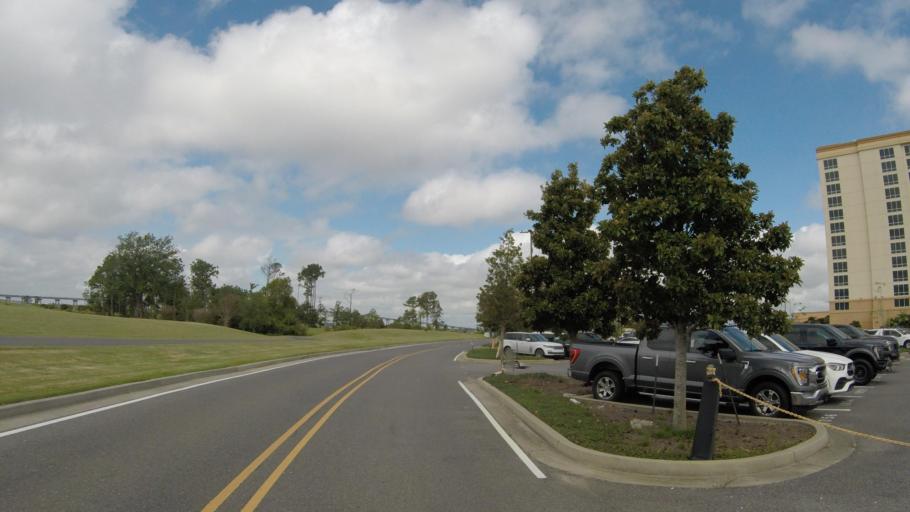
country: US
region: Louisiana
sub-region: Calcasieu Parish
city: Prien
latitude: 30.2023
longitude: -93.2642
